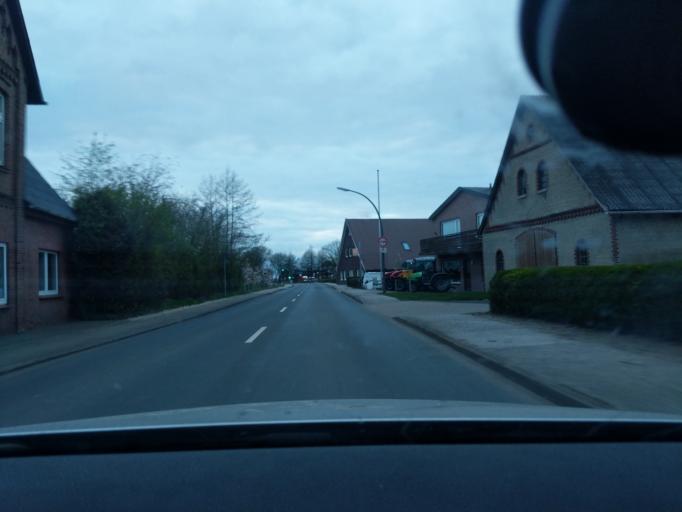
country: DE
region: Lower Saxony
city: Neu Wulmstorf
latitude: 53.5172
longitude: 9.7843
